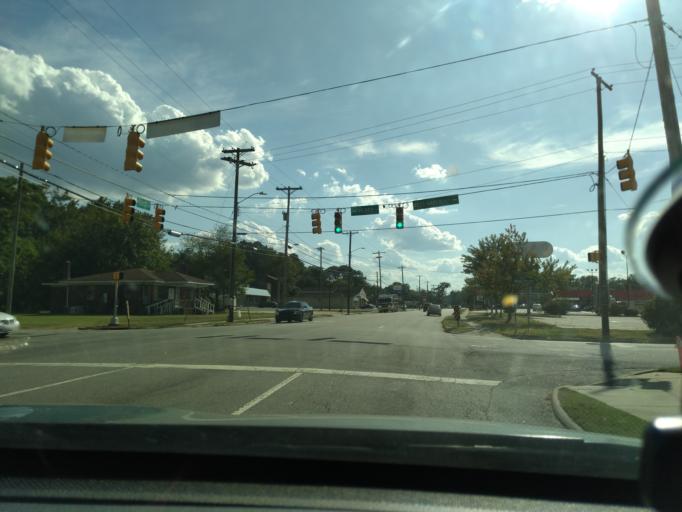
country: US
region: North Carolina
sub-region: Nash County
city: Rocky Mount
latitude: 35.9332
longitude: -77.8104
